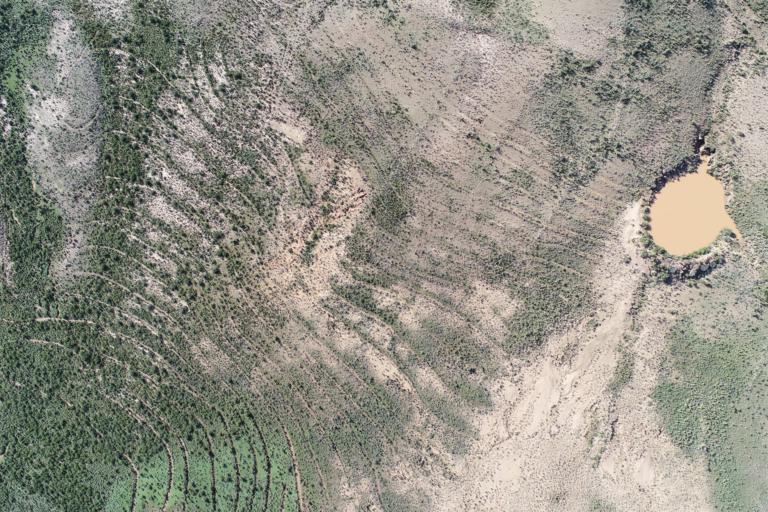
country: BO
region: La Paz
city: Curahuara de Carangas
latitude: -17.3044
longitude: -68.5071
